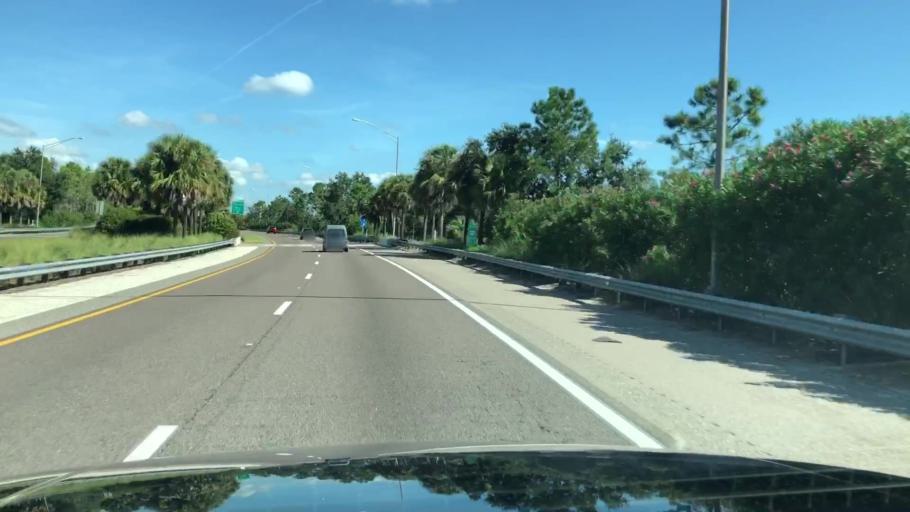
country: US
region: Florida
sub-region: Orange County
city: Gotha
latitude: 28.5345
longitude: -81.5575
